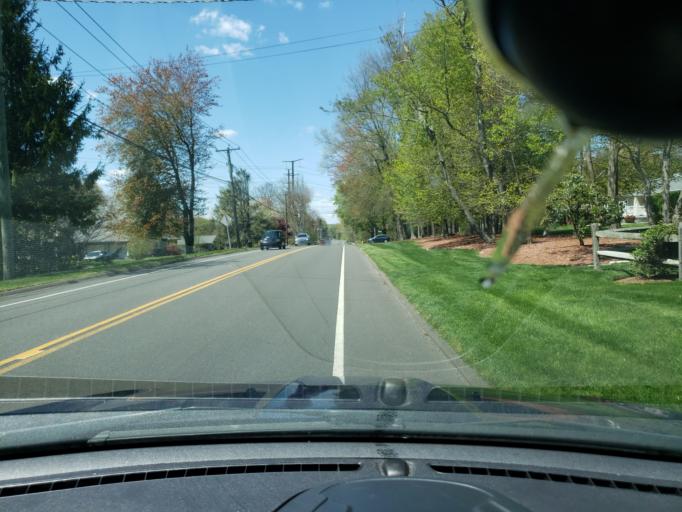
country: US
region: Connecticut
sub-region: New Haven County
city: Orange
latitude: 41.2812
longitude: -73.0090
